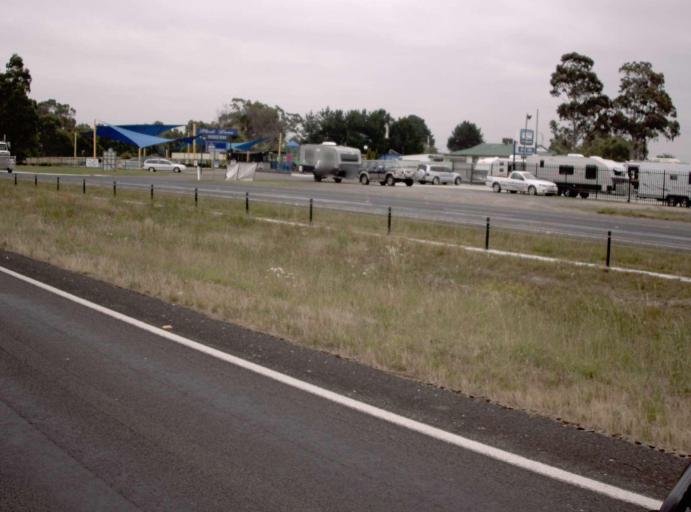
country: AU
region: Victoria
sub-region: Latrobe
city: Traralgon
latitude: -38.2159
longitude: 146.4793
